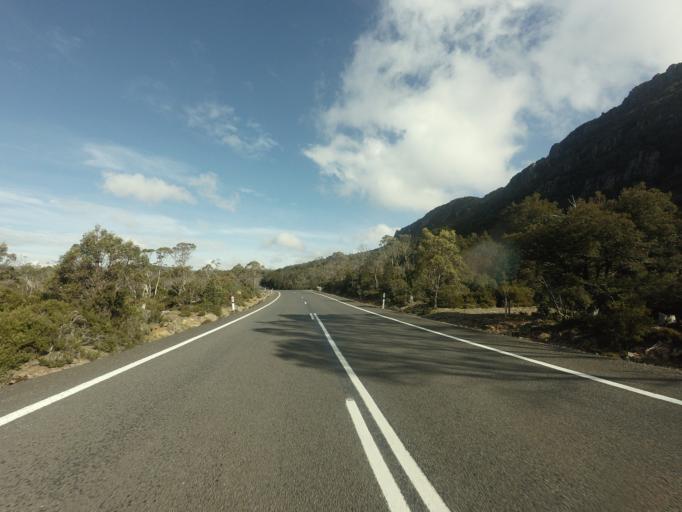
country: AU
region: Tasmania
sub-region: Meander Valley
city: Deloraine
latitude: -41.7225
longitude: 146.7244
